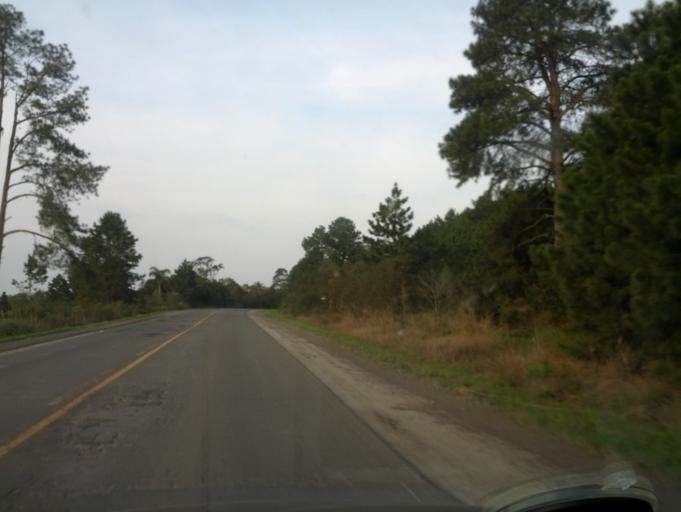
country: BR
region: Santa Catarina
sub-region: Otacilio Costa
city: Otacilio Costa
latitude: -27.3069
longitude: -50.1113
